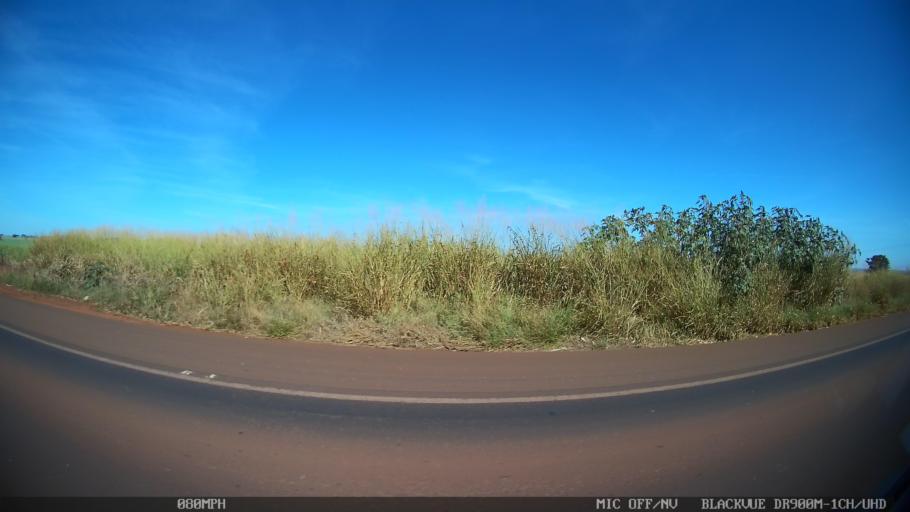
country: BR
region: Sao Paulo
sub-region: Sao Joaquim Da Barra
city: Sao Joaquim da Barra
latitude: -20.5445
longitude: -47.7842
